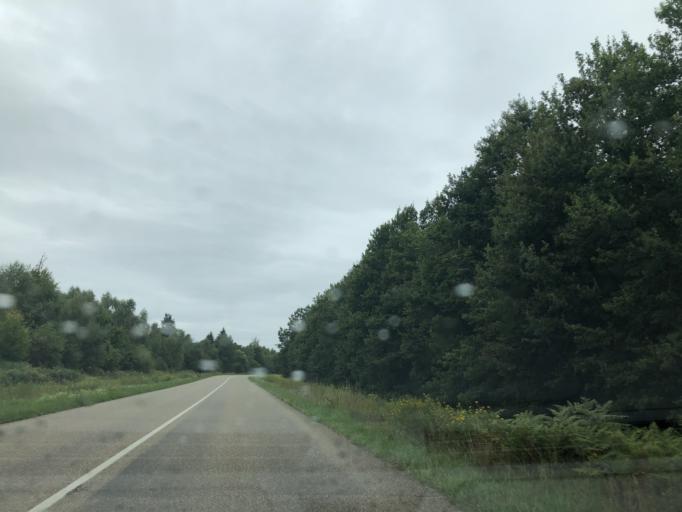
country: DE
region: Rheinland-Pfalz
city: Scheibenhardt
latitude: 48.9831
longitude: 8.1166
